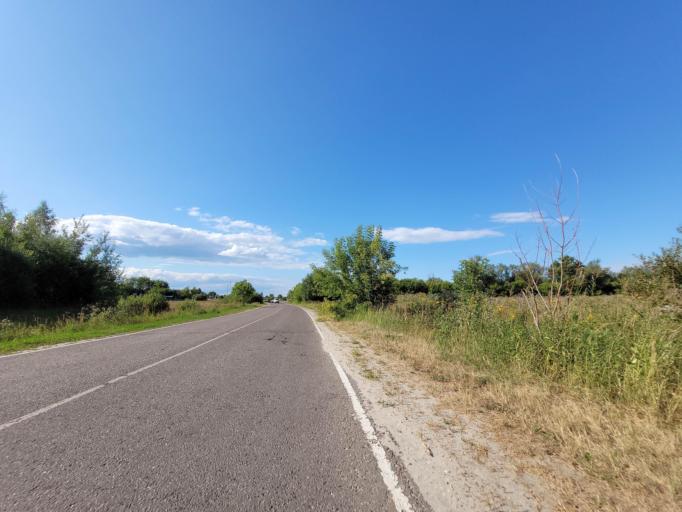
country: RU
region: Moskovskaya
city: Konobeyevo
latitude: 55.4031
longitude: 38.7082
